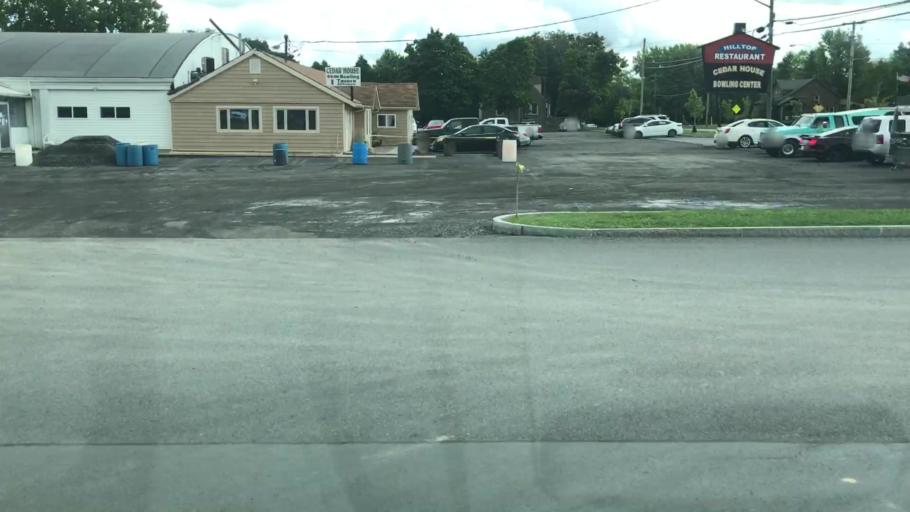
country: US
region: New York
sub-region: Onondaga County
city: Skaneateles
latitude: 42.9444
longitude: -76.4463
